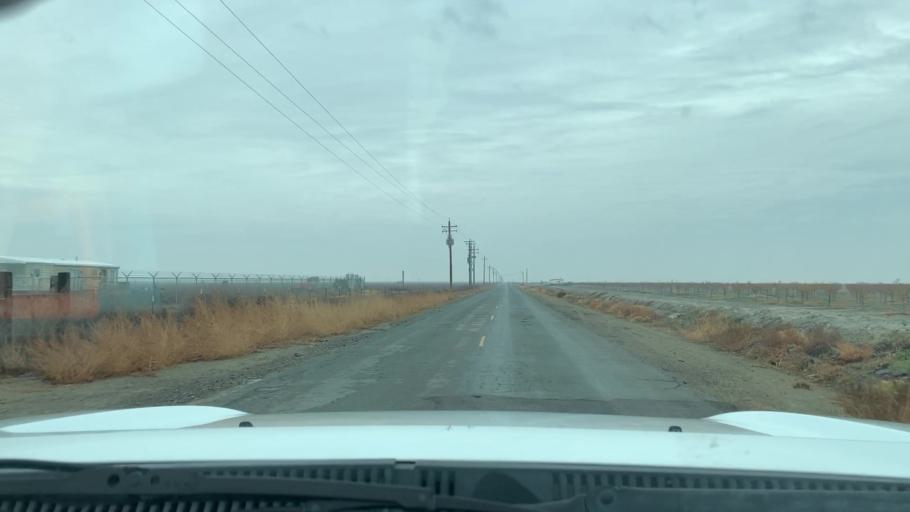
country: US
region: California
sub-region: Tulare County
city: Alpaugh
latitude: 35.7609
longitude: -119.5168
